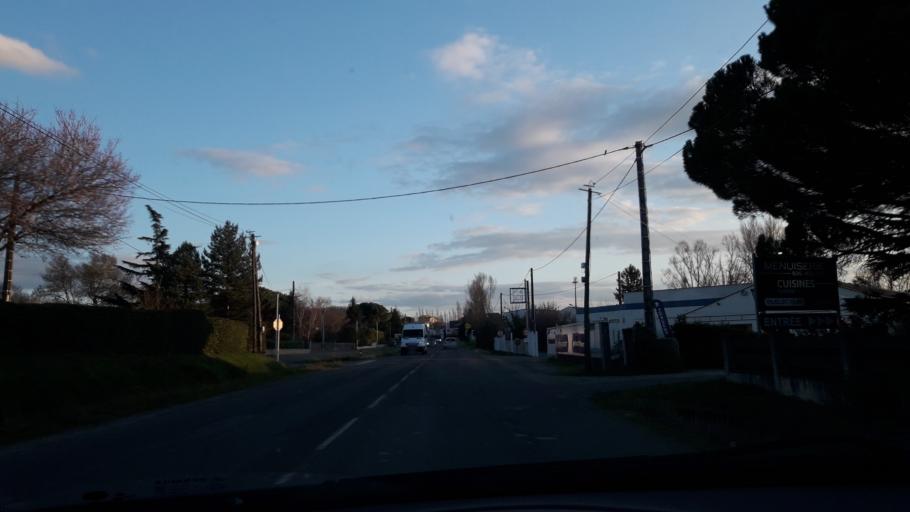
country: FR
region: Midi-Pyrenees
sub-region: Departement du Gers
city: Pujaudran
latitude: 43.6078
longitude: 1.1001
